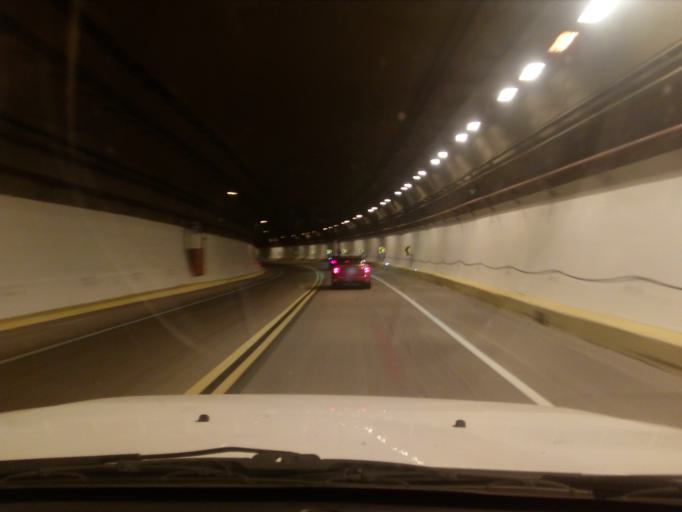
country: MX
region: Durango
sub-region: Pueblo Nuevo
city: La Ciudad
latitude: 23.5773
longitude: -105.7283
